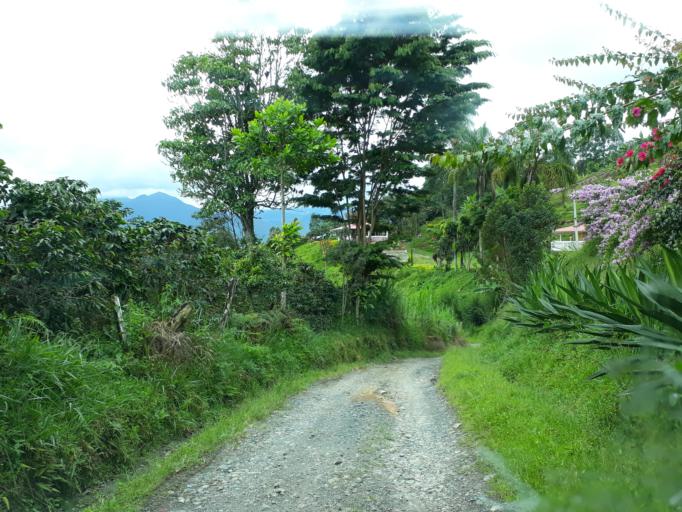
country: CO
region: Cundinamarca
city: Pacho
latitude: 5.1595
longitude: -74.2373
